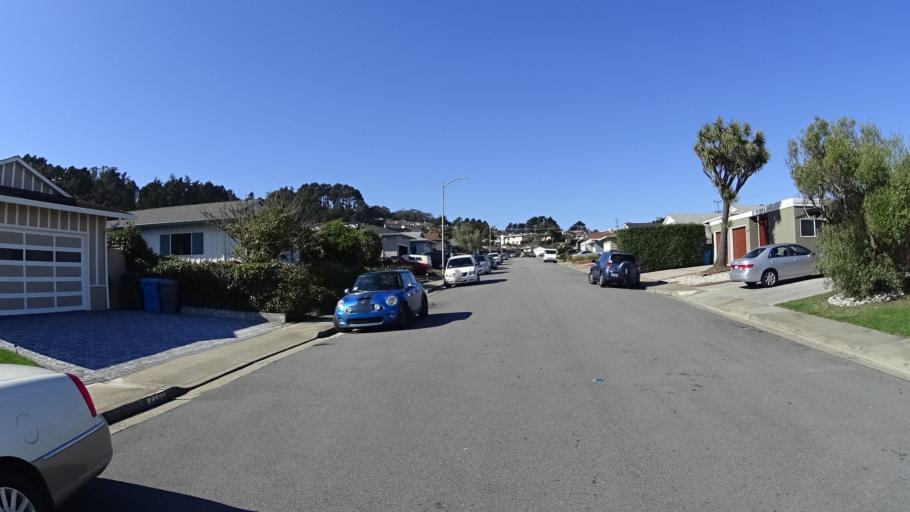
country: US
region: California
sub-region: San Mateo County
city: Colma
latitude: 37.6386
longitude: -122.4575
